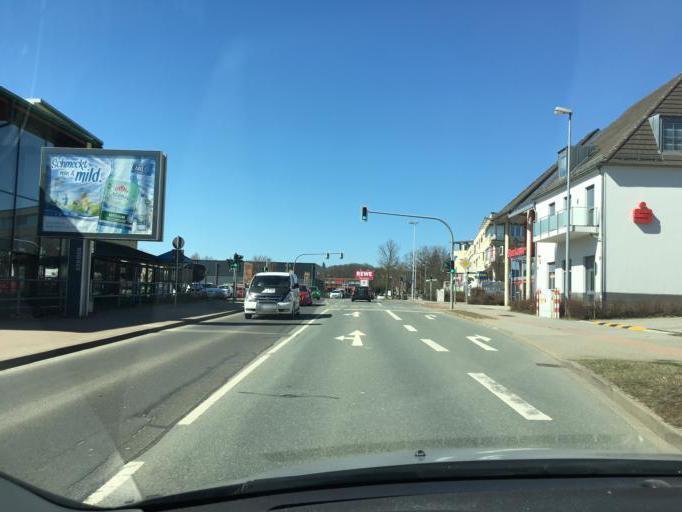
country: DE
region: Saxony
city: Neukirchen
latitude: 50.8250
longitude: 12.8336
